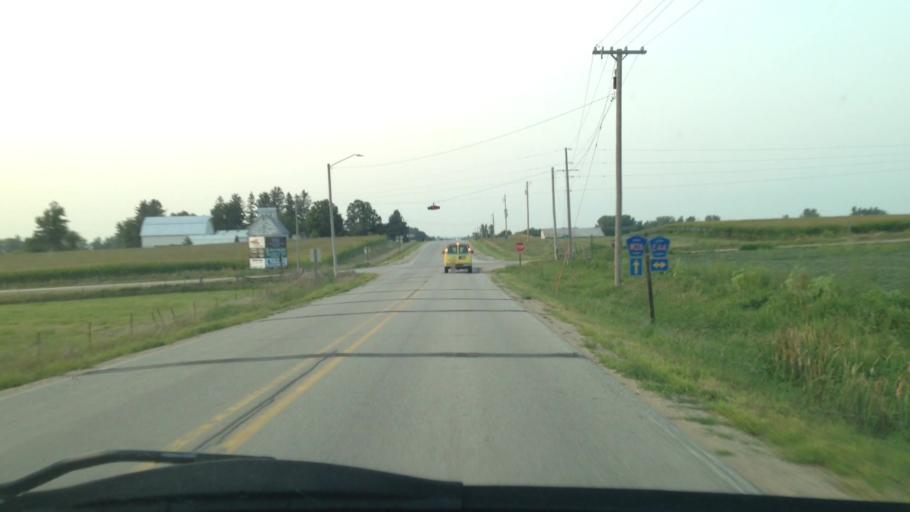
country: US
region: Iowa
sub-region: Benton County
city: Atkins
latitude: 41.9917
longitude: -91.8732
